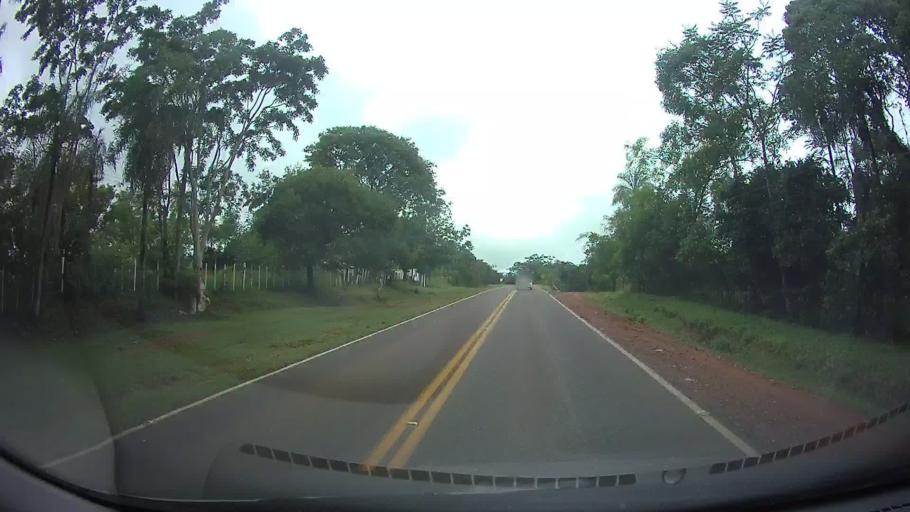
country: PY
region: Paraguari
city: Acahay
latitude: -25.9327
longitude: -57.1053
